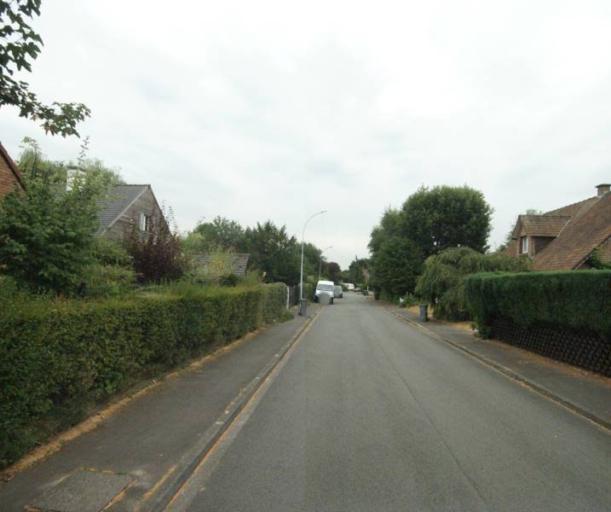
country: FR
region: Nord-Pas-de-Calais
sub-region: Departement du Nord
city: Bondues
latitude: 50.6996
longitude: 3.0922
